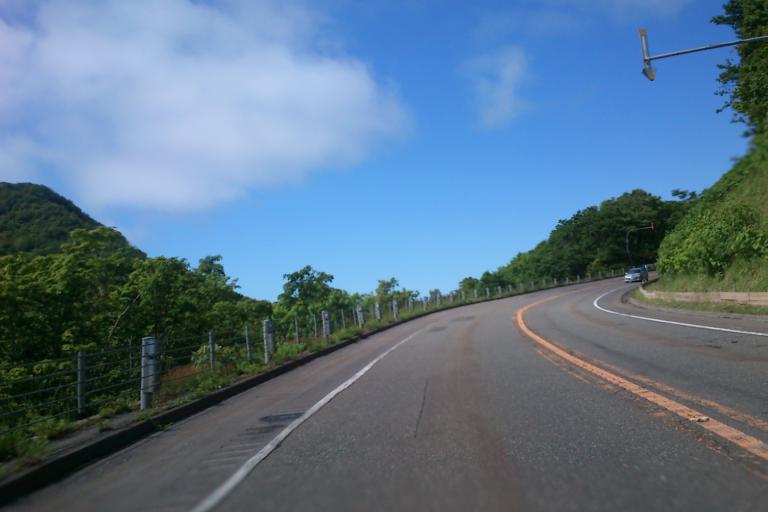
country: JP
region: Hokkaido
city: Ishikari
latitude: 43.4824
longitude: 141.3973
